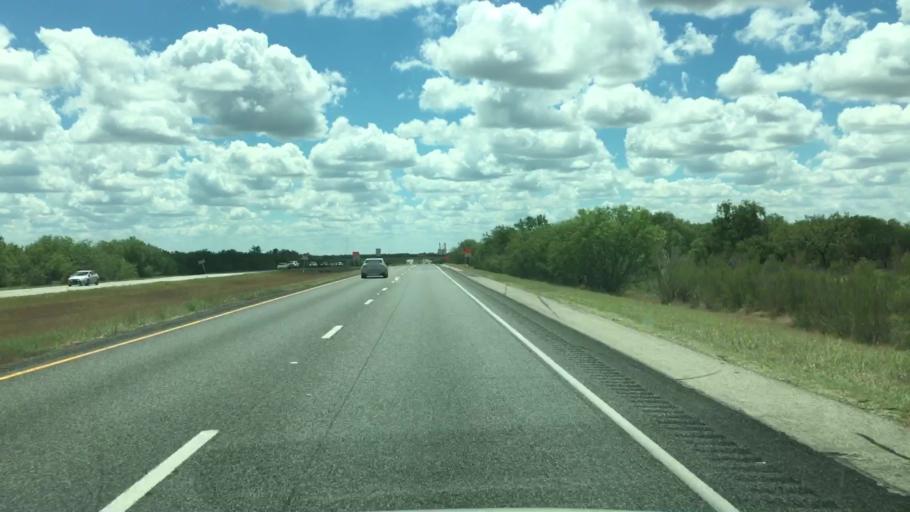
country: US
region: Texas
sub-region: Atascosa County
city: Pleasanton
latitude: 28.9801
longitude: -98.4335
